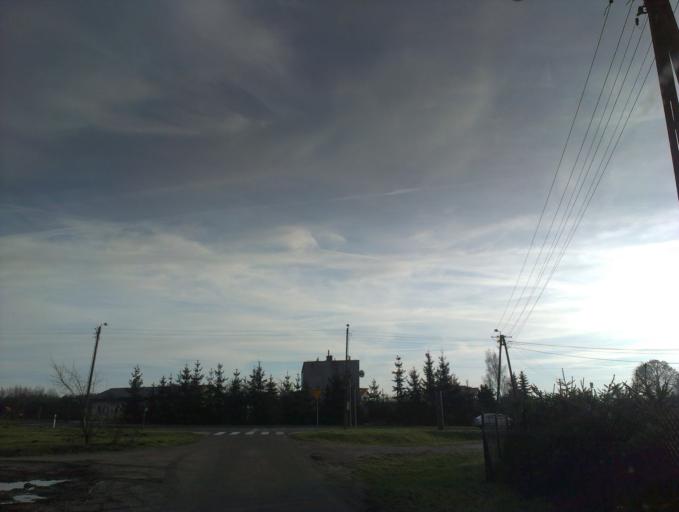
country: PL
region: Pomeranian Voivodeship
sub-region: Powiat czluchowski
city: Debrzno
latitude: 53.6145
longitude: 17.1877
